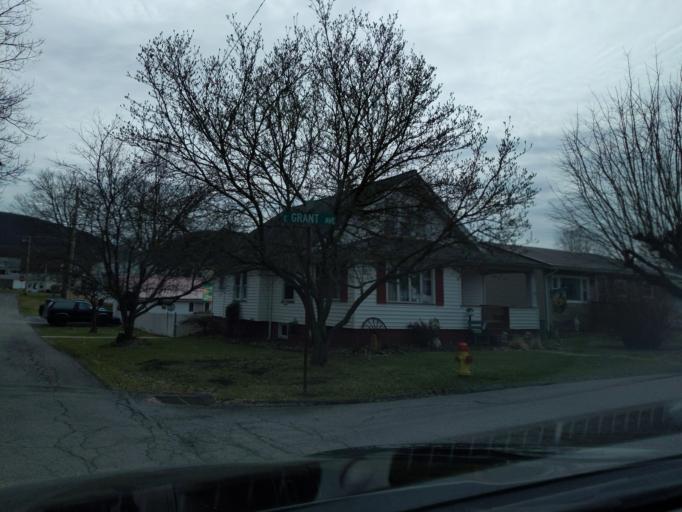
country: US
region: Pennsylvania
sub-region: Blair County
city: Greenwood
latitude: 40.5236
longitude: -78.3743
